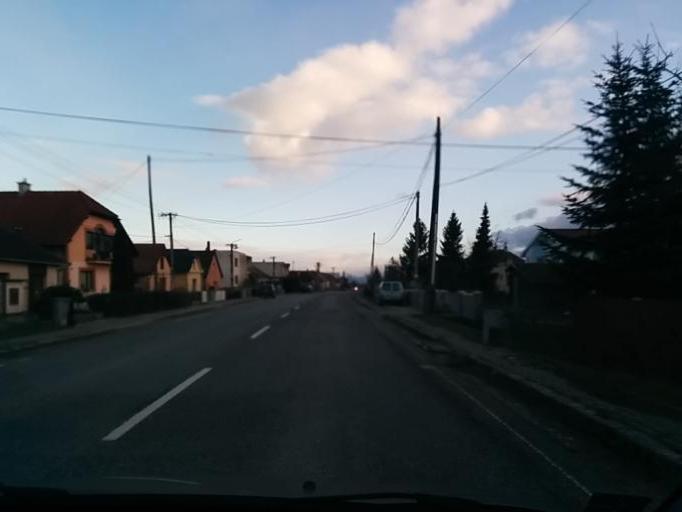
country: SK
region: Nitriansky
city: Cachtice
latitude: 48.6870
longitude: 17.8474
